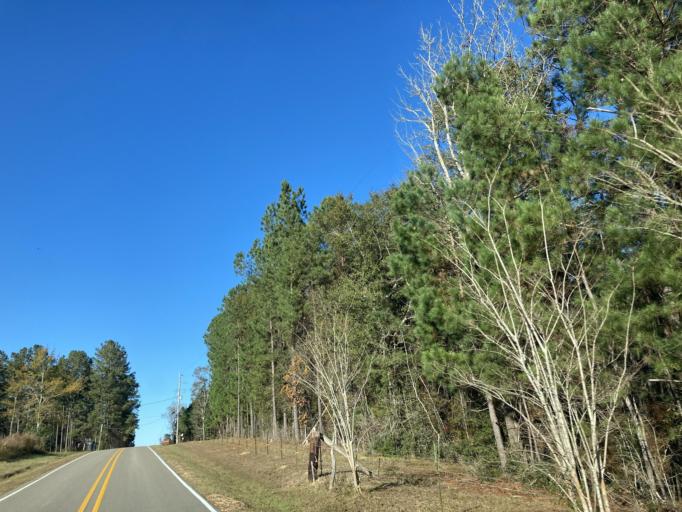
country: US
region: Mississippi
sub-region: Lamar County
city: Sumrall
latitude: 31.3644
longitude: -89.5693
